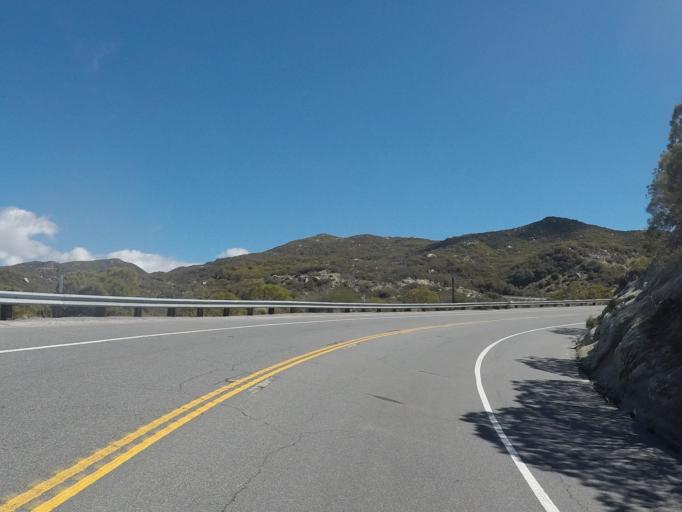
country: US
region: California
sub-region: Riverside County
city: Idyllwild-Pine Cove
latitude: 33.6988
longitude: -116.7602
